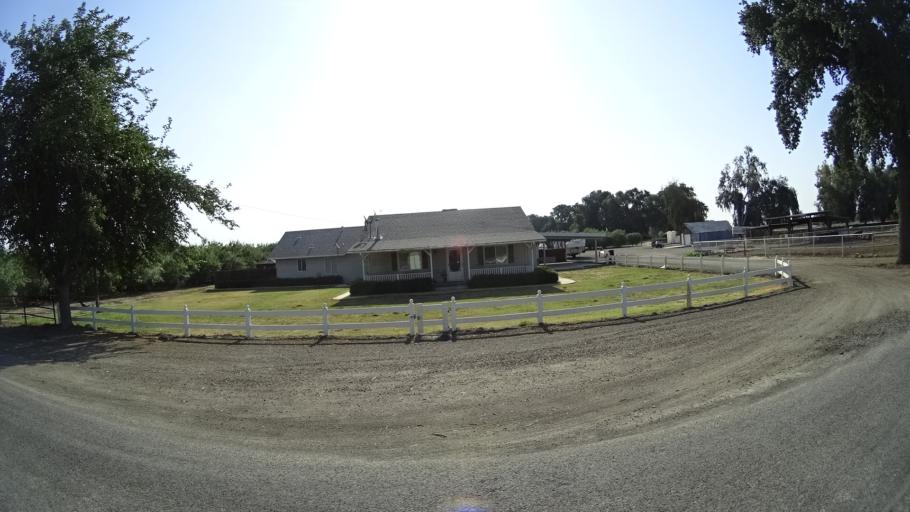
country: US
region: California
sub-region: Kings County
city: Lemoore
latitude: 36.3683
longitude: -119.8162
